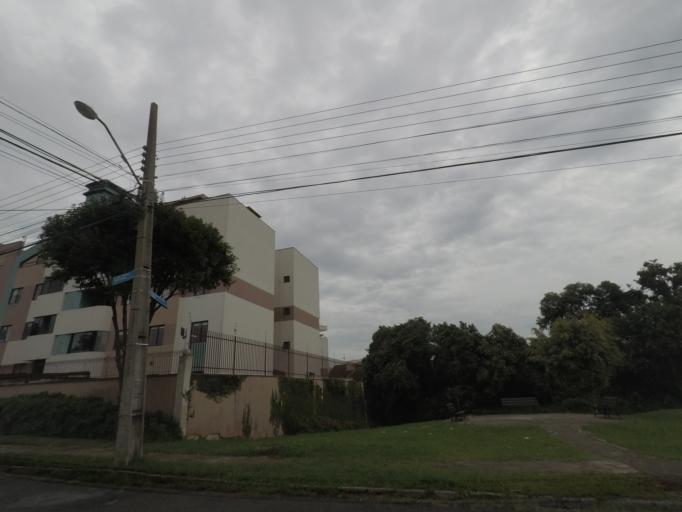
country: BR
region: Parana
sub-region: Curitiba
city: Curitiba
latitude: -25.4712
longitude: -49.3062
